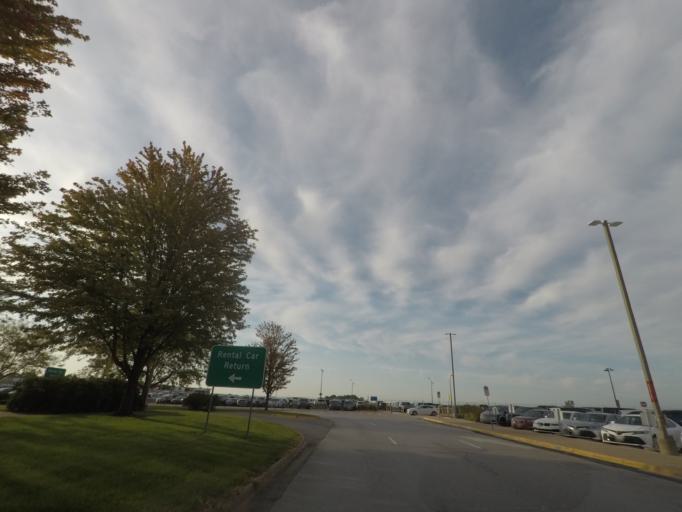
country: US
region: Iowa
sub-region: Warren County
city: Norwalk
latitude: 41.5317
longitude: -93.6480
